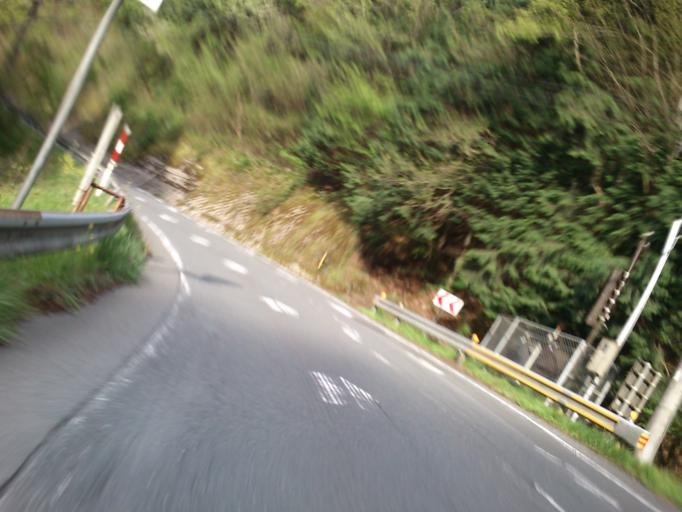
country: JP
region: Kyoto
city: Ayabe
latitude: 35.2389
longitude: 135.3023
